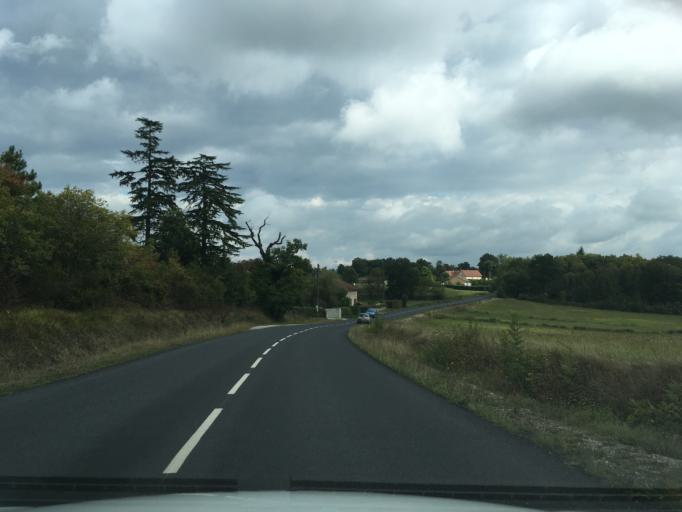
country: FR
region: Limousin
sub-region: Departement de la Correze
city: Brive-la-Gaillarde
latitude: 45.1054
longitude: 1.5419
